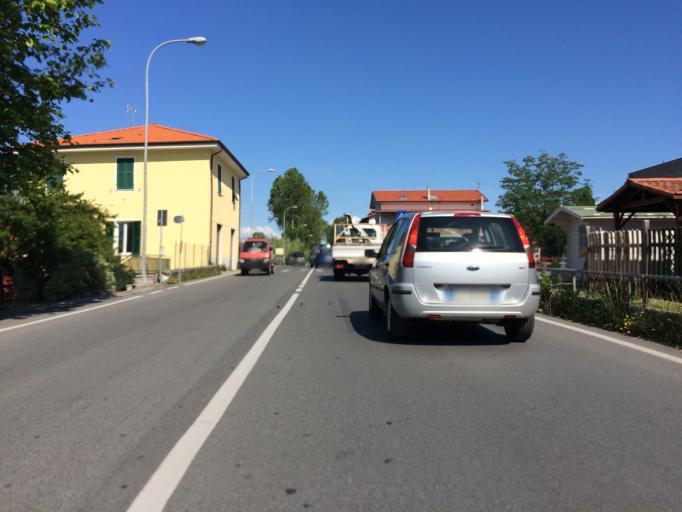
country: IT
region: Tuscany
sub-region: Provincia di Massa-Carrara
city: Borghetto-Melara
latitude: 44.0965
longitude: 9.9875
